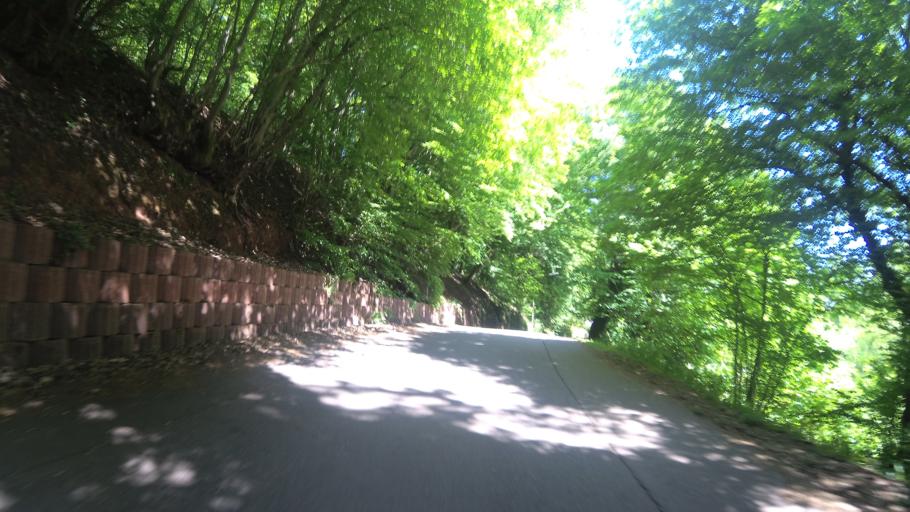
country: DE
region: Saarland
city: Mettlach
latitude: 49.4802
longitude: 6.5943
